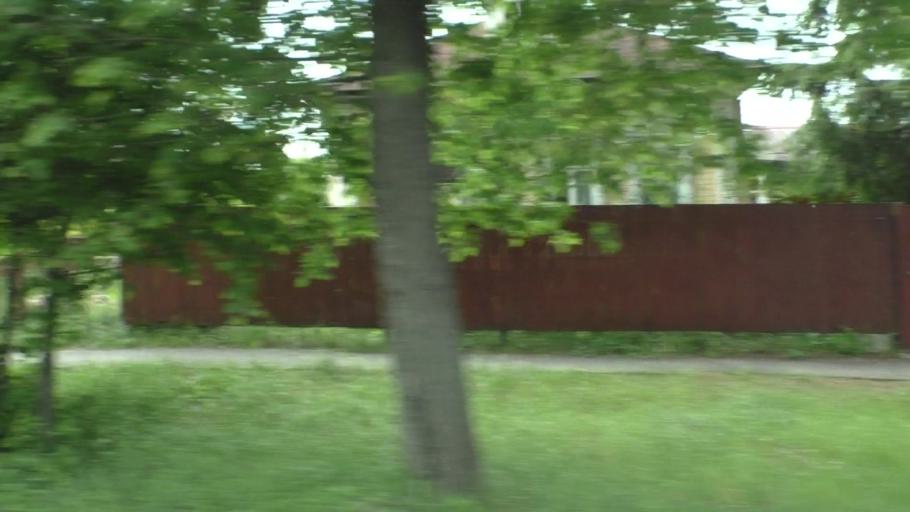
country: RU
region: Moskovskaya
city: Imeni Tsyurupy
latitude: 55.5074
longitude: 38.7661
